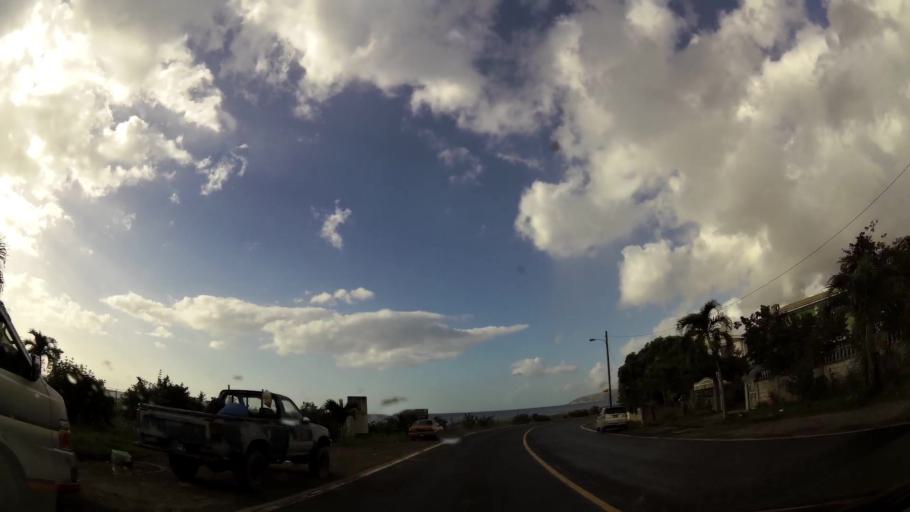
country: DM
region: Saint Paul
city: Mahaut
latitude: 15.3358
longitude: -61.3913
